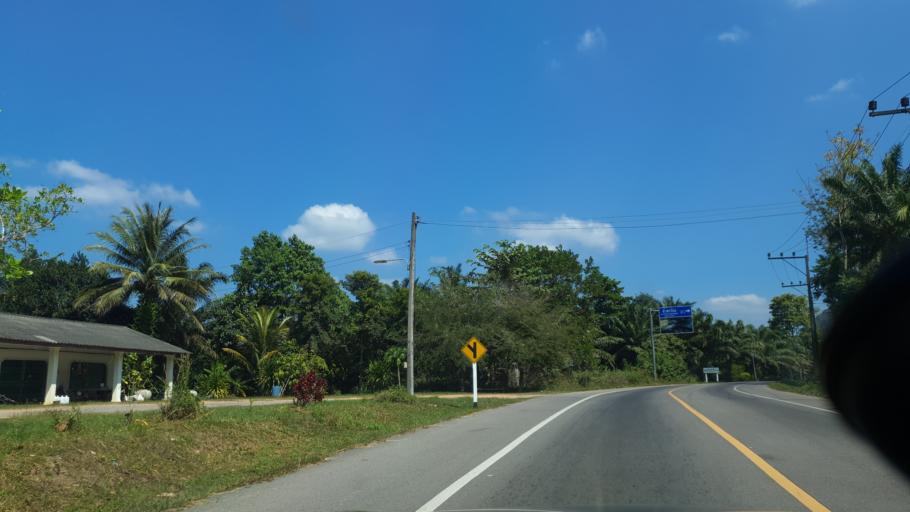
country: TH
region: Krabi
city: Khlong Thom
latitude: 7.9527
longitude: 99.2002
